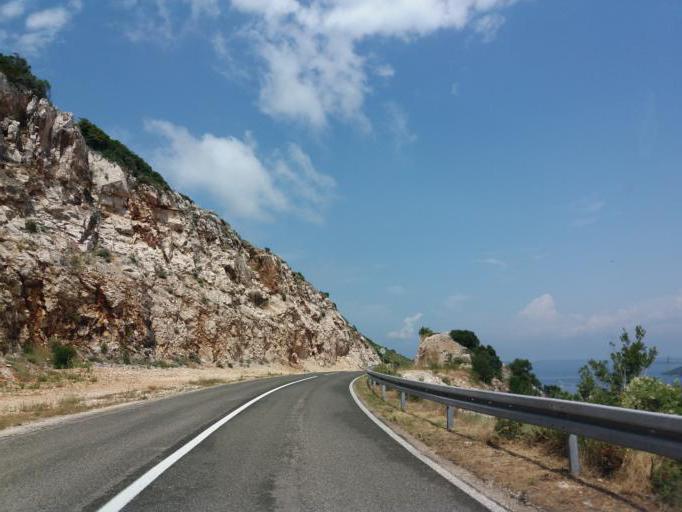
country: HR
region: Zadarska
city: Ugljan
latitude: 44.0104
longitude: 15.0459
